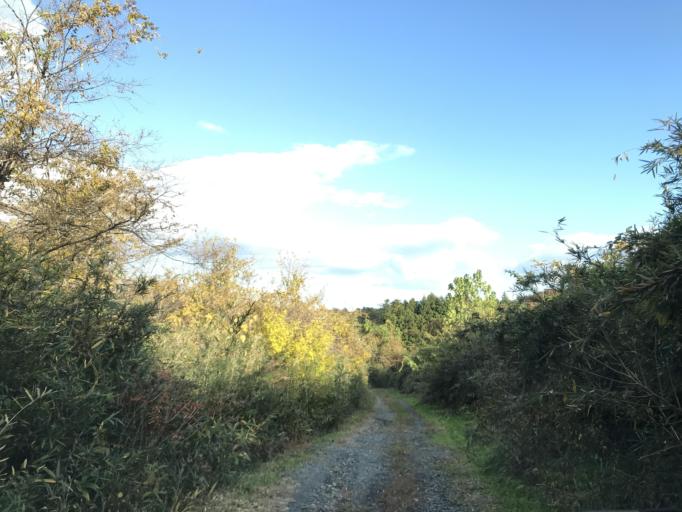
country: JP
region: Iwate
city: Ichinoseki
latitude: 38.8737
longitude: 141.1375
